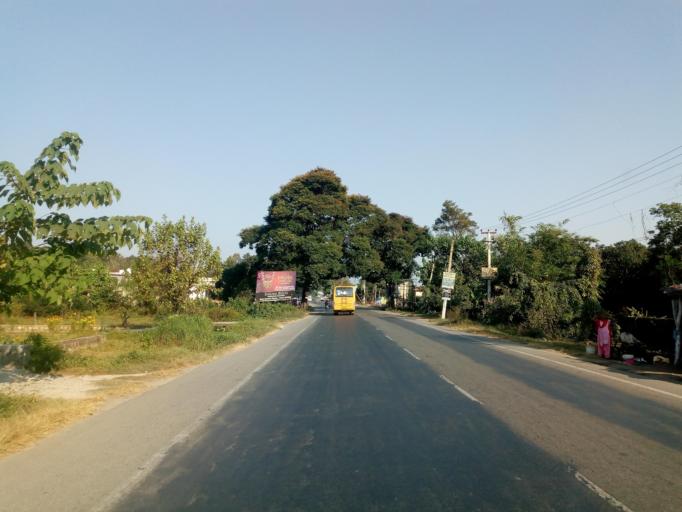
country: IN
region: Uttarakhand
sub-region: Dehradun
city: Dehradun
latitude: 30.3442
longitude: 77.9221
